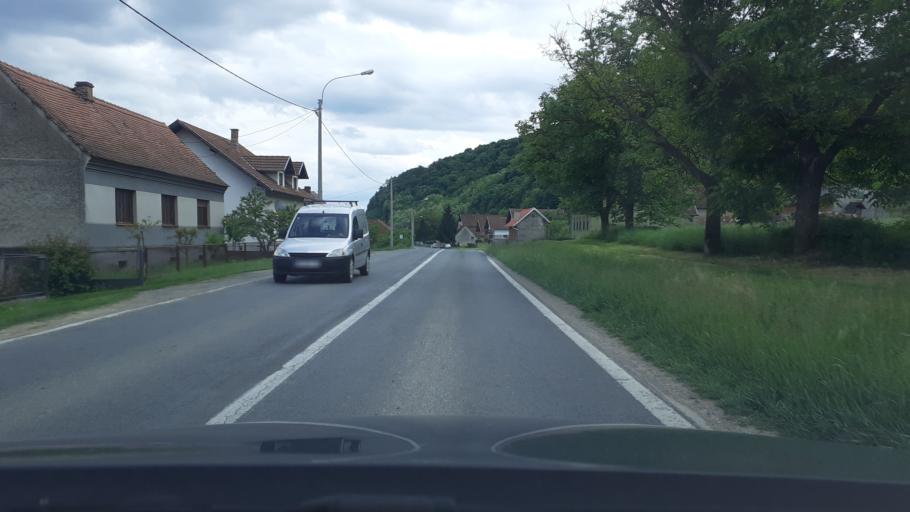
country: HR
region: Pozesko-Slavonska
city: Gradac
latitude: 45.3163
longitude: 17.7754
